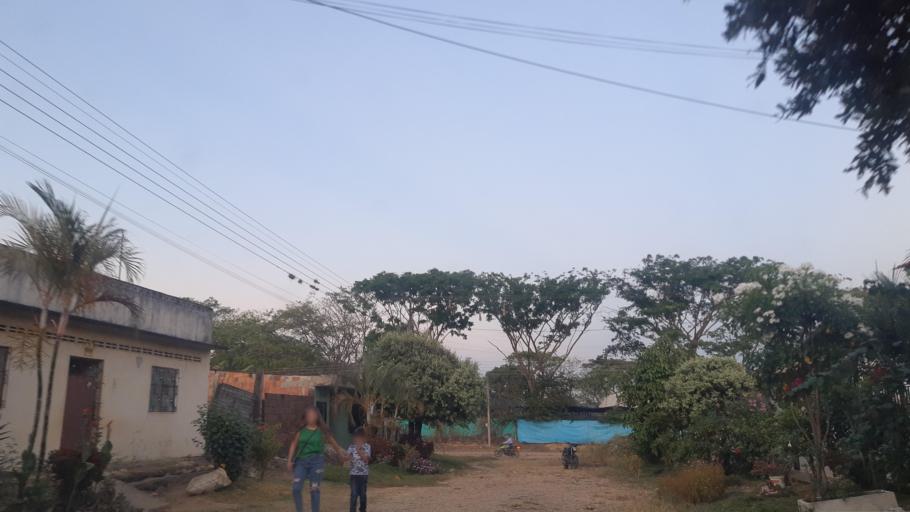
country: CO
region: Arauca
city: Tame
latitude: 6.4568
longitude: -71.7295
